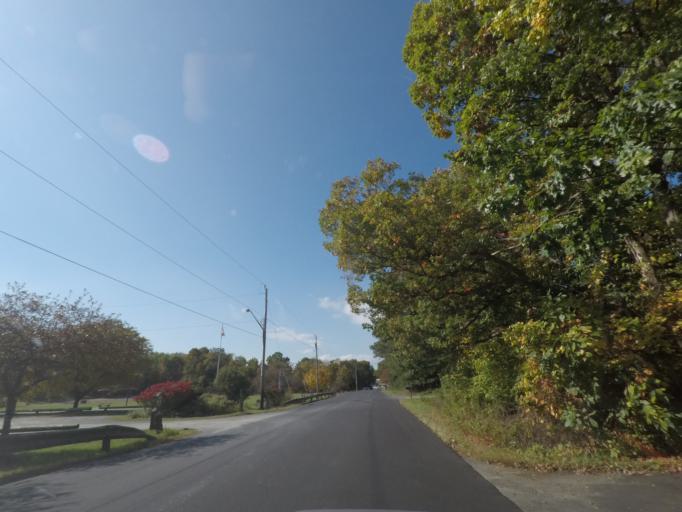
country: US
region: New York
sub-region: Rensselaer County
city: Averill Park
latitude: 42.6430
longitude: -73.5679
